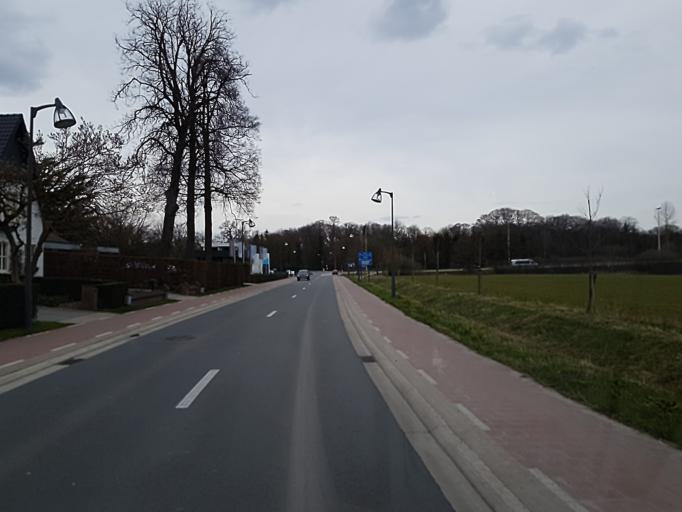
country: BE
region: Flanders
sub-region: Provincie Antwerpen
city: Turnhout
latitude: 51.3367
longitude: 4.9447
